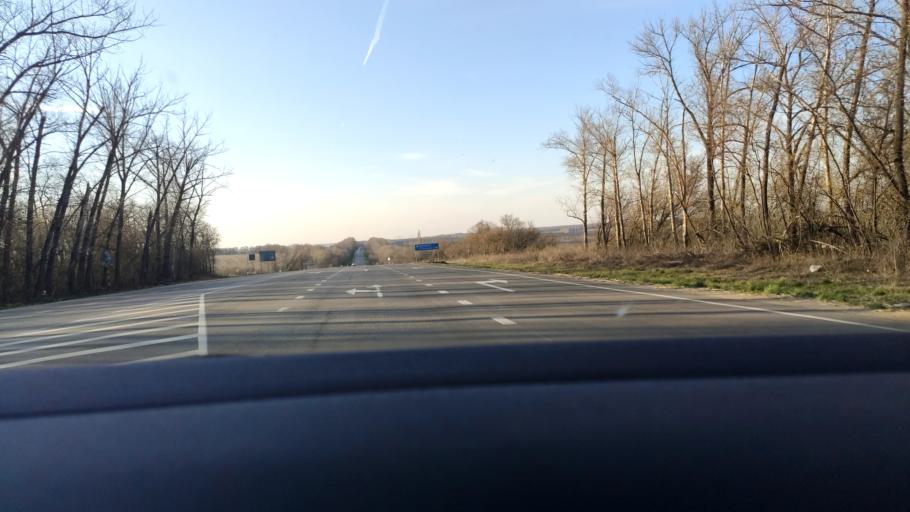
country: RU
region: Voronezj
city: Uryv-Pokrovka
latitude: 51.2019
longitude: 39.0797
